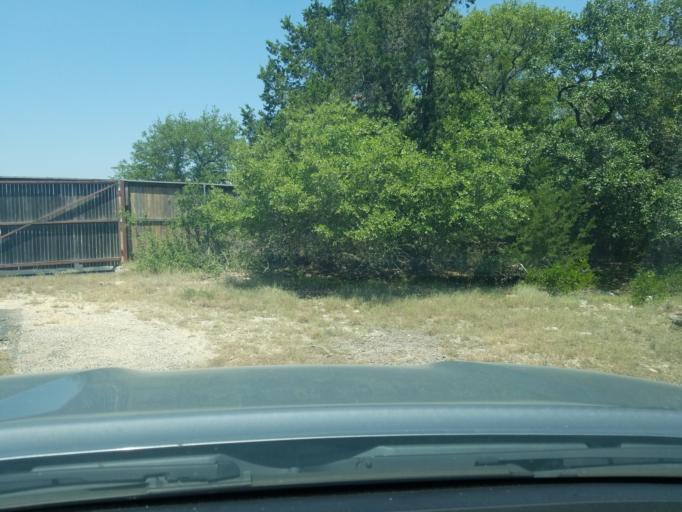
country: US
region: Texas
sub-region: Bexar County
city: Timberwood Park
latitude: 29.7121
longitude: -98.4938
